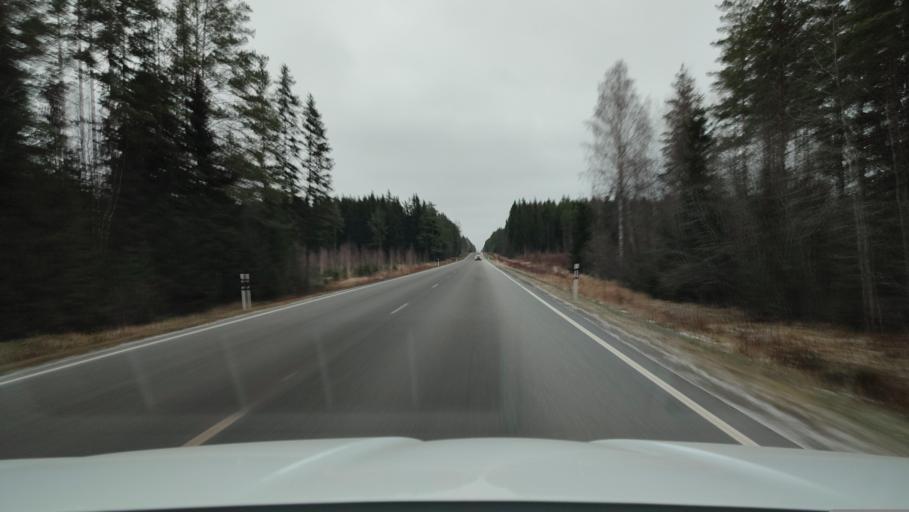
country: FI
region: Ostrobothnia
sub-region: Sydosterbotten
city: Naerpes
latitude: 62.5556
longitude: 21.4761
